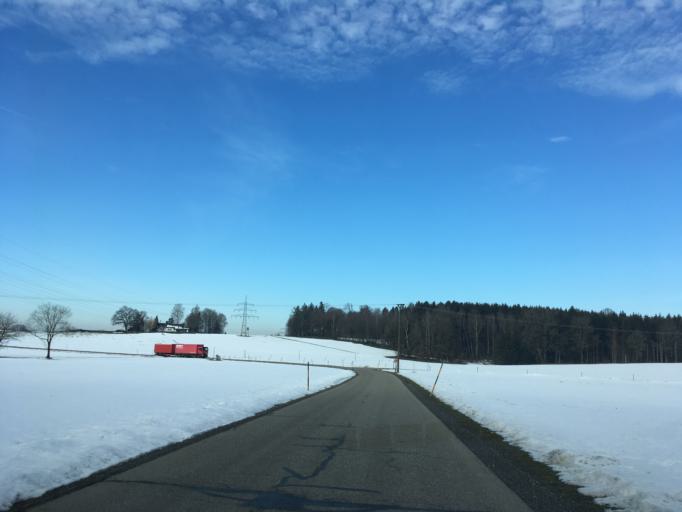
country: DE
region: Bavaria
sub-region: Upper Bavaria
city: Stephanskirchen
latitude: 47.8784
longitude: 12.1605
